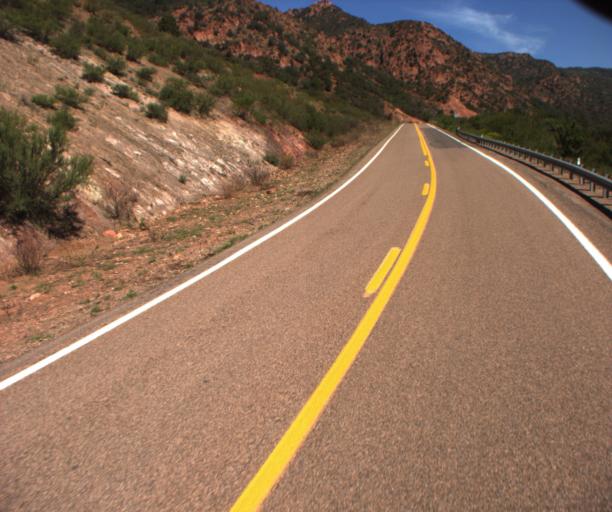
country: US
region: Arizona
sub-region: Greenlee County
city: Morenci
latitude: 33.1460
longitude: -109.3744
